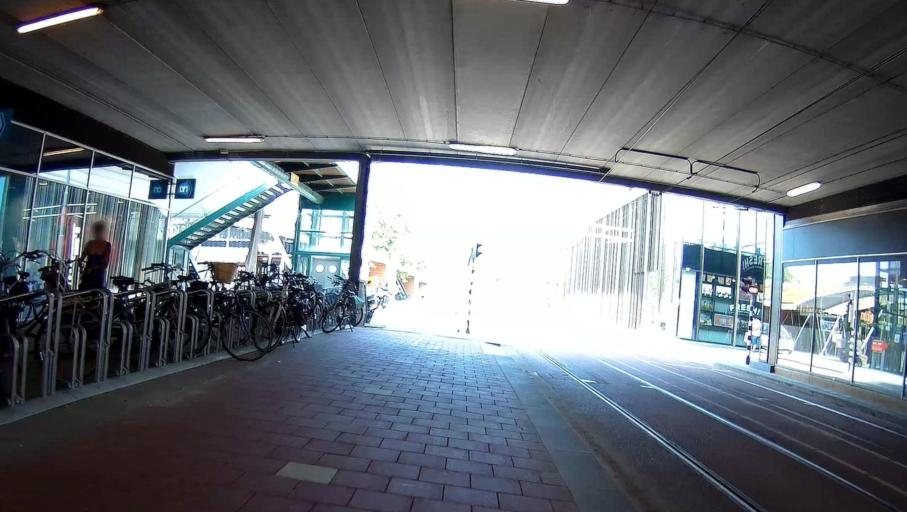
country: NL
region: South Holland
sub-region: Gemeente Leidschendam-Voorburg
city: Voorburg
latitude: 52.0873
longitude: 4.3835
